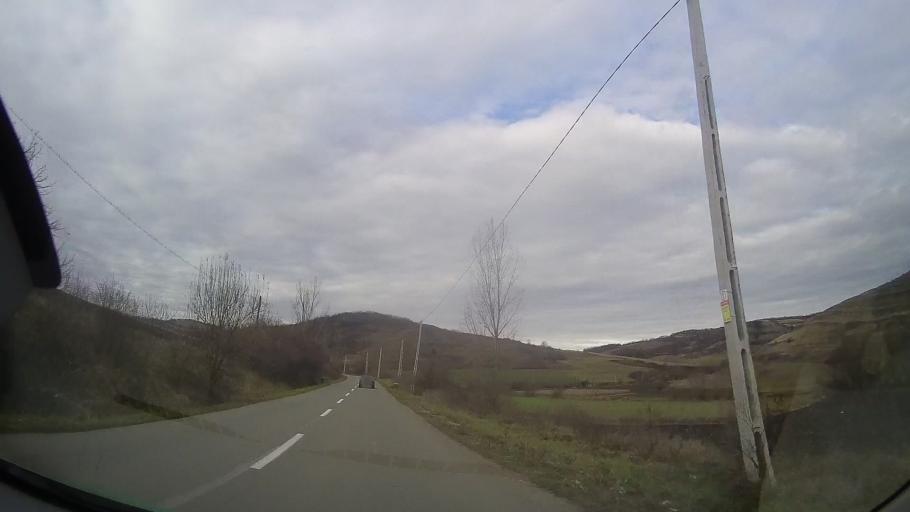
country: RO
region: Bistrita-Nasaud
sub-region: Comuna Milas
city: Milas
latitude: 46.8370
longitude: 24.4476
